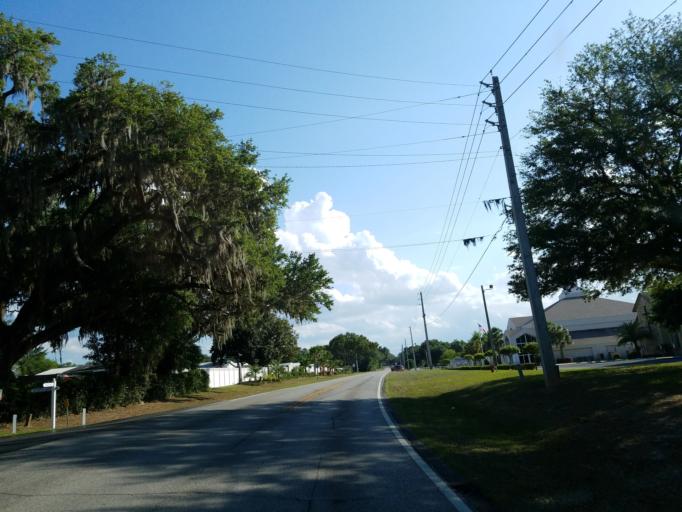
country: US
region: Florida
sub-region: Lake County
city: Fruitland Park
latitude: 28.8556
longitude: -81.8885
